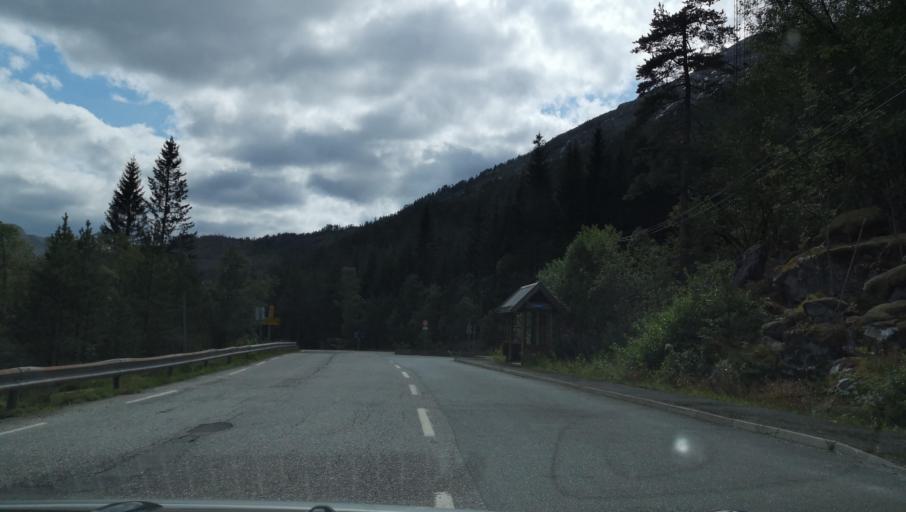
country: NO
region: Hordaland
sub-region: Modalen
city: Mo
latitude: 60.7848
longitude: 5.8389
